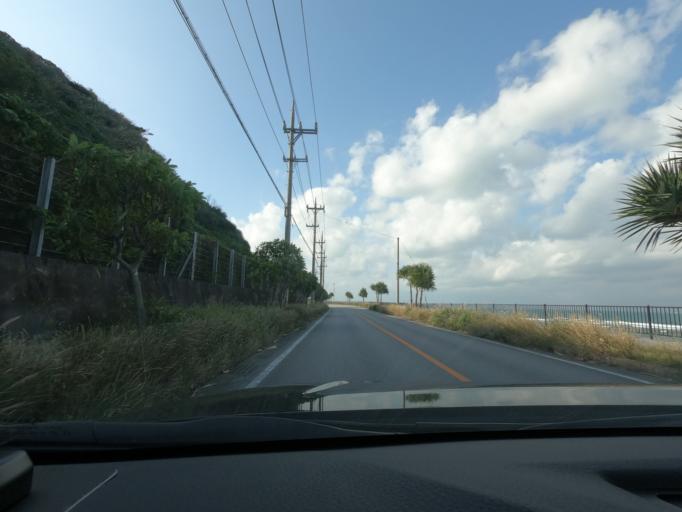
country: JP
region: Okinawa
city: Nago
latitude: 26.7615
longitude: 128.1908
